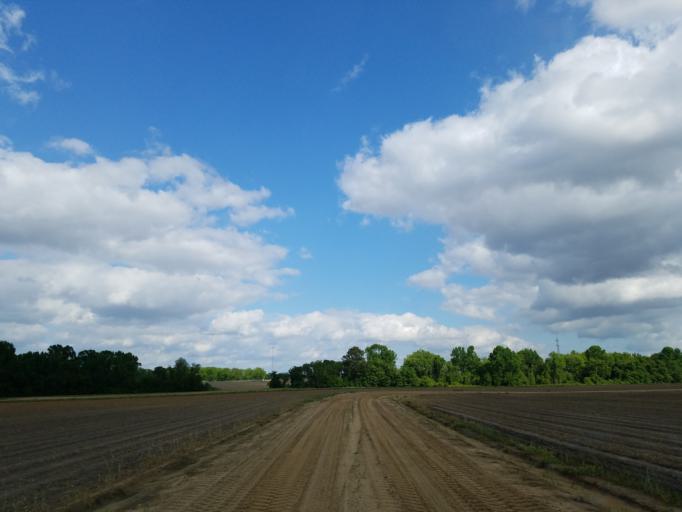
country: US
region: Georgia
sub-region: Dooly County
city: Vienna
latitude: 32.1752
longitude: -83.7766
